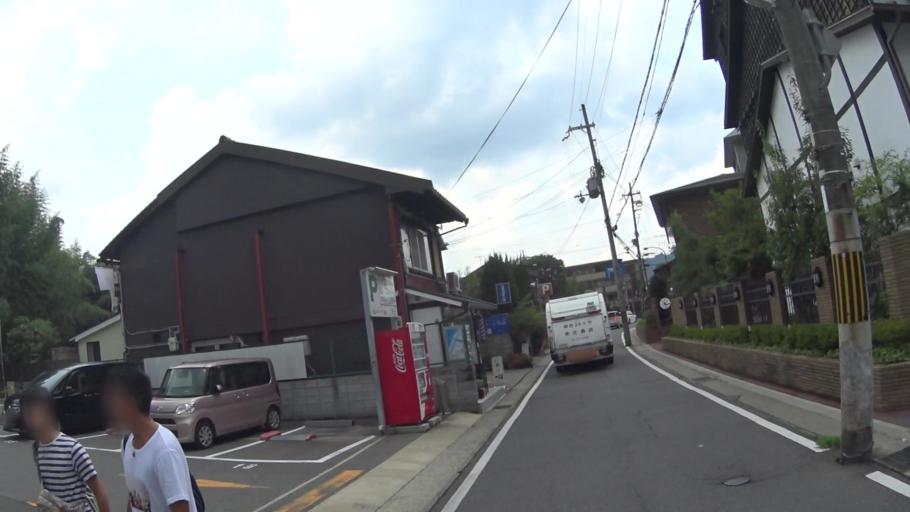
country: JP
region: Kyoto
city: Muko
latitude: 35.0190
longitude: 135.6761
